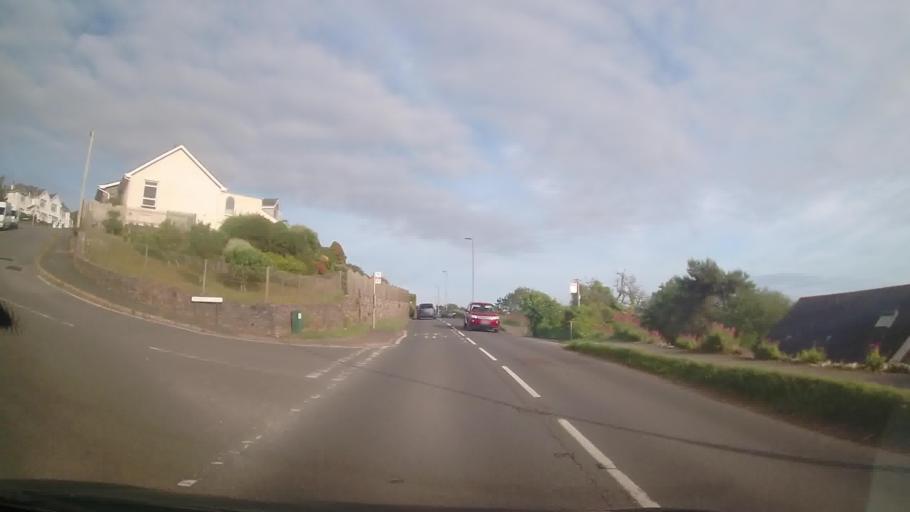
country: GB
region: England
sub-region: Devon
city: Kingsbridge
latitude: 50.2748
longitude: -3.7708
